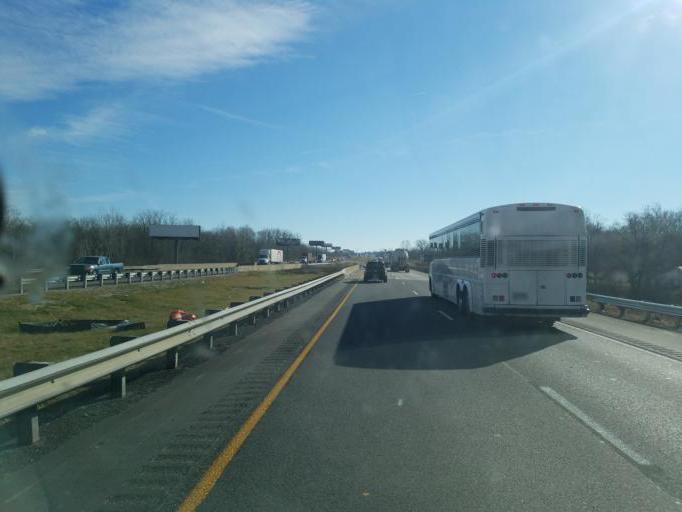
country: US
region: Ohio
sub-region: Preble County
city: New Paris
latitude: 39.8471
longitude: -84.8317
